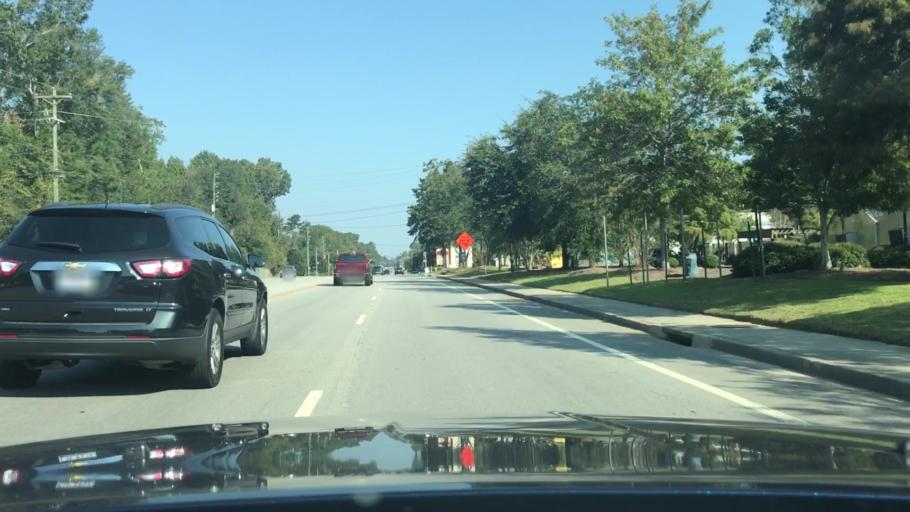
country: US
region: South Carolina
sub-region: Dorchester County
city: Centerville
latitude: 32.9758
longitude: -80.1719
